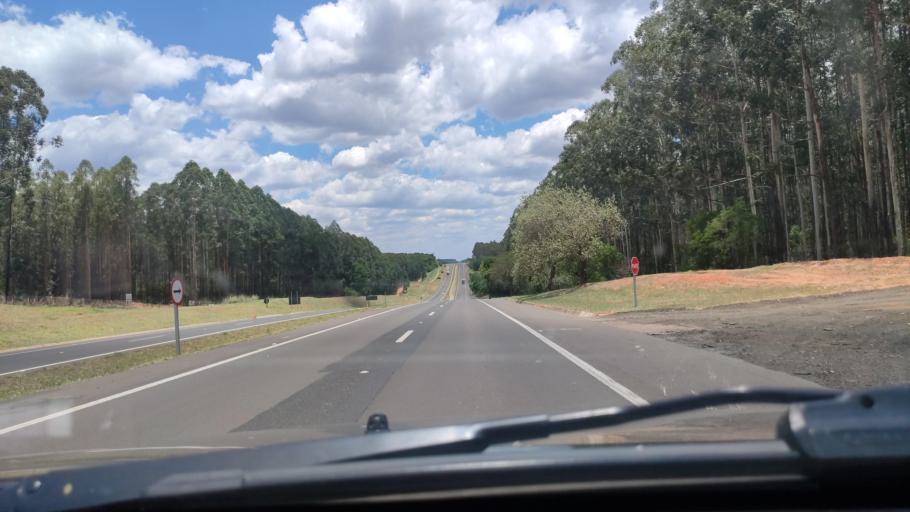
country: BR
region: Sao Paulo
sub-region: Duartina
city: Duartina
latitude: -22.4907
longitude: -49.2506
